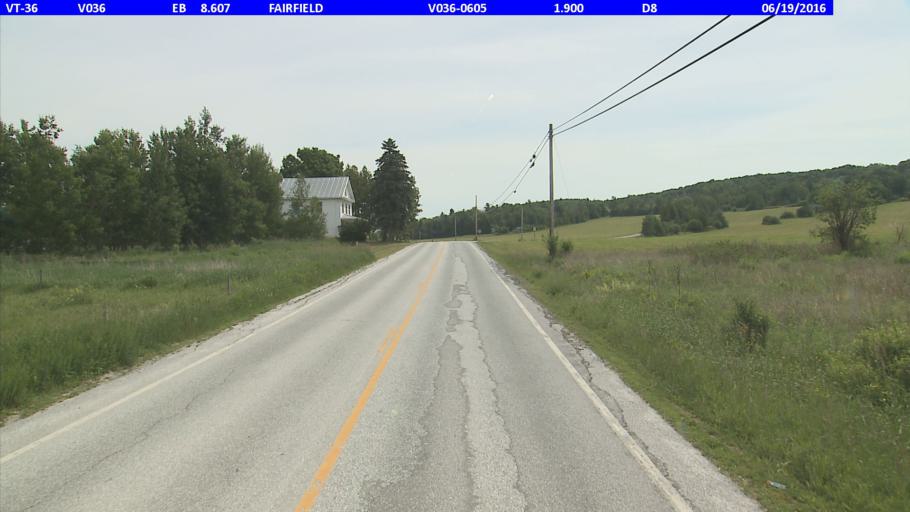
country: US
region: Vermont
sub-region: Franklin County
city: Saint Albans
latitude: 44.7883
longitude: -72.9938
